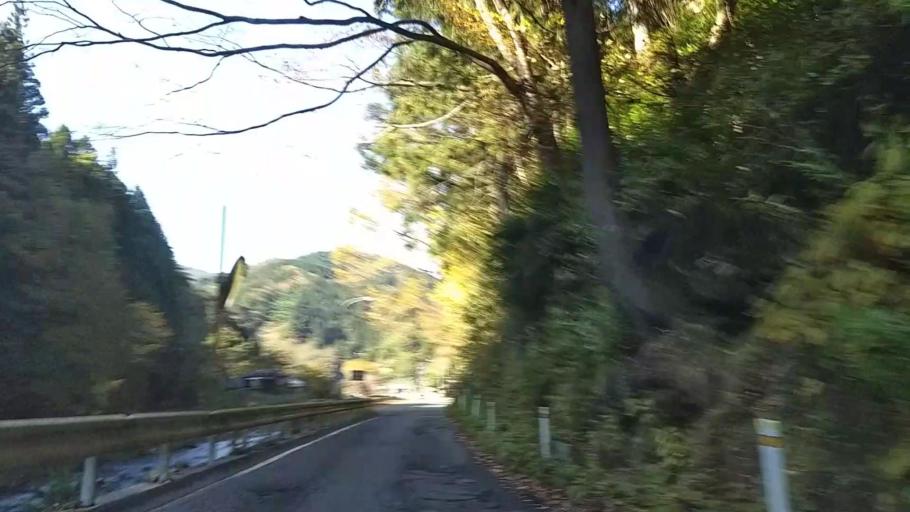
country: JP
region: Yamanashi
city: Otsuki
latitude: 35.7063
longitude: 139.0100
